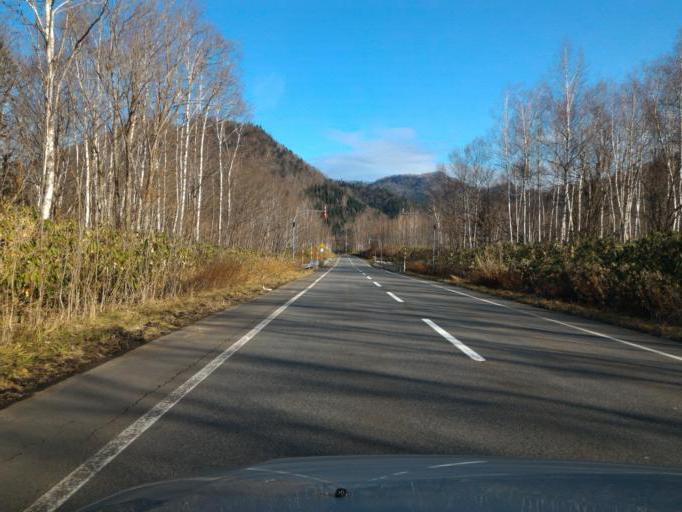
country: JP
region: Hokkaido
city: Ashibetsu
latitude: 43.3244
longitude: 142.1512
